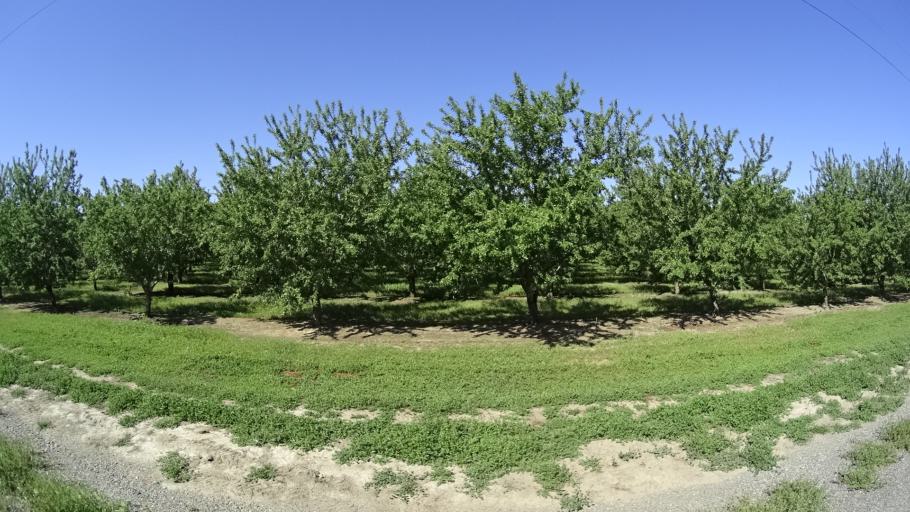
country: US
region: California
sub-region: Glenn County
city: Hamilton City
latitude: 39.7277
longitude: -122.0214
